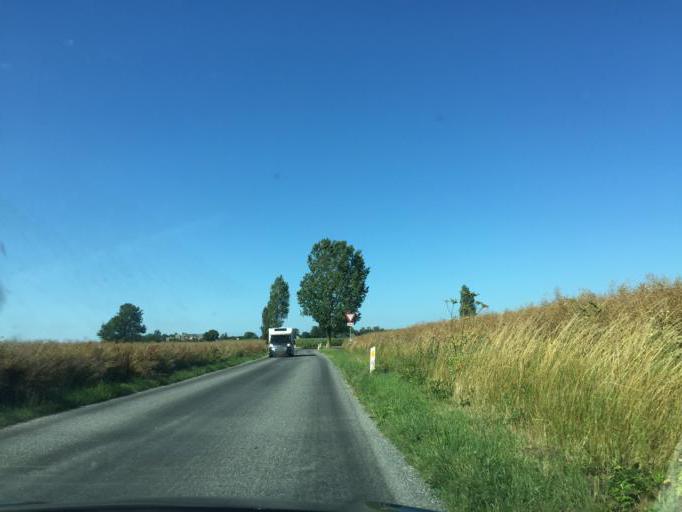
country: DK
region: South Denmark
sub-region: Nordfyns Kommune
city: Sonderso
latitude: 55.4903
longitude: 10.2860
